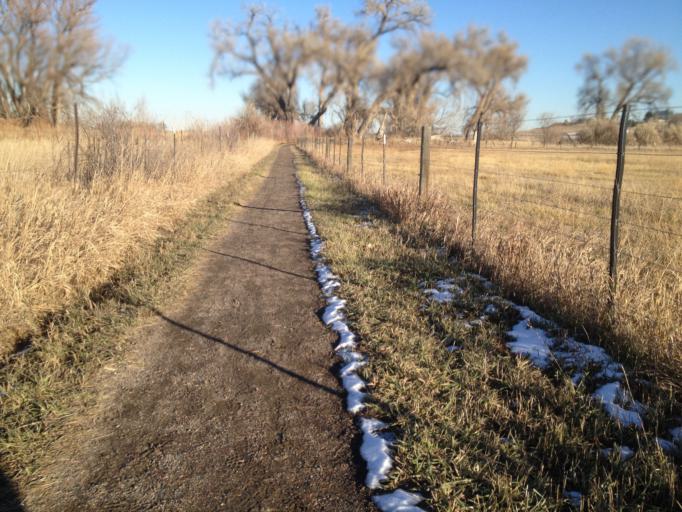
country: US
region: Colorado
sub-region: Boulder County
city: Gunbarrel
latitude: 40.0440
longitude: -105.1454
